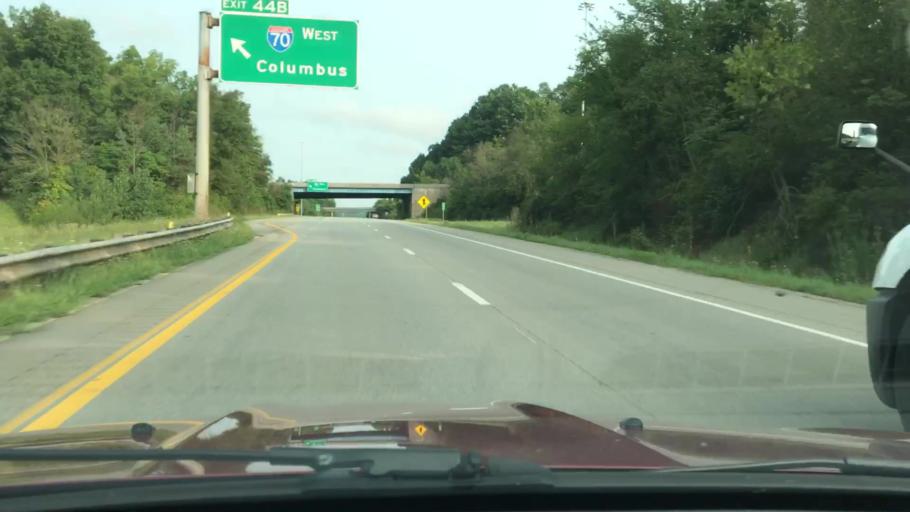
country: US
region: Ohio
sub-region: Guernsey County
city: Byesville
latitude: 39.9968
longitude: -81.5543
